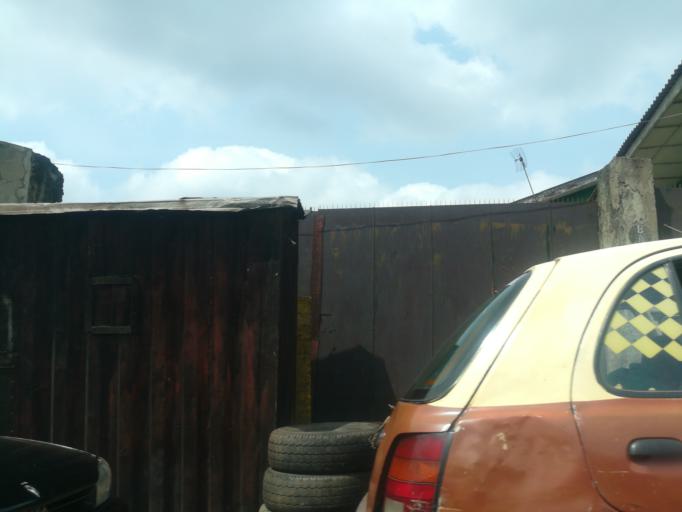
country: NG
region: Oyo
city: Ibadan
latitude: 7.4116
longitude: 3.9516
